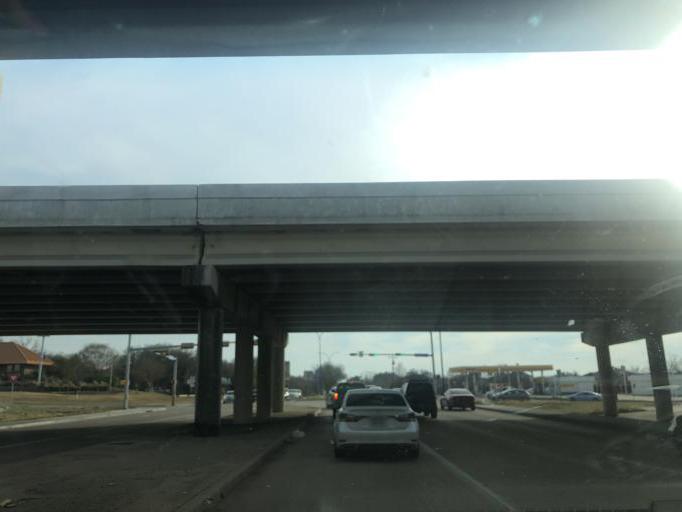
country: US
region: Texas
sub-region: Tarrant County
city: Dalworthington Gardens
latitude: 32.6746
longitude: -97.1497
